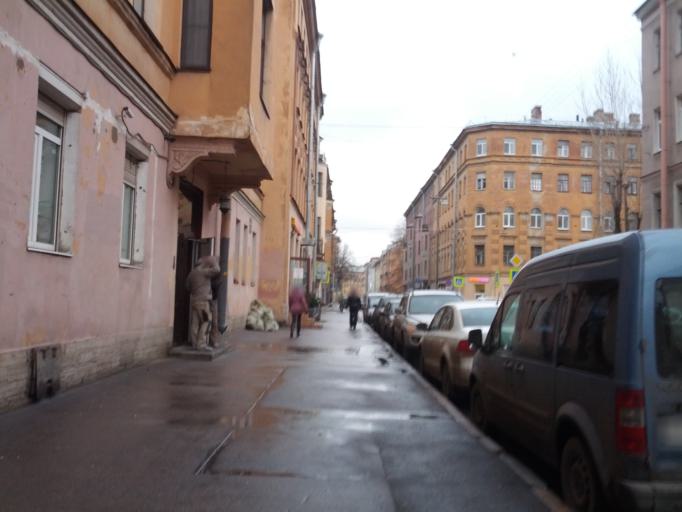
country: RU
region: St.-Petersburg
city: Petrogradka
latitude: 59.9576
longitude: 30.3058
